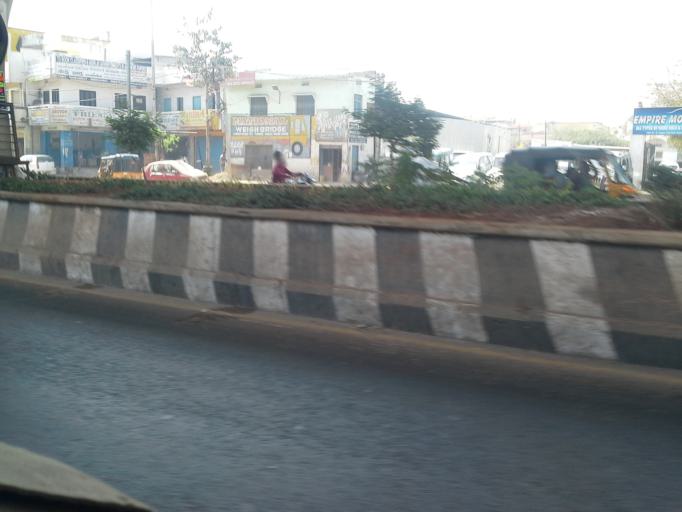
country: IN
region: Telangana
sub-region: Hyderabad
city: Hyderabad
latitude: 17.3786
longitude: 78.4295
